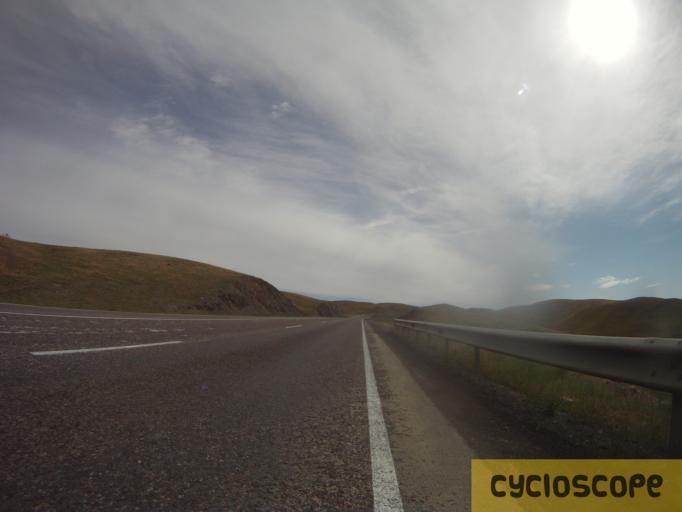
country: KZ
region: Zhambyl
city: Georgiyevka
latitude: 43.2585
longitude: 74.8222
